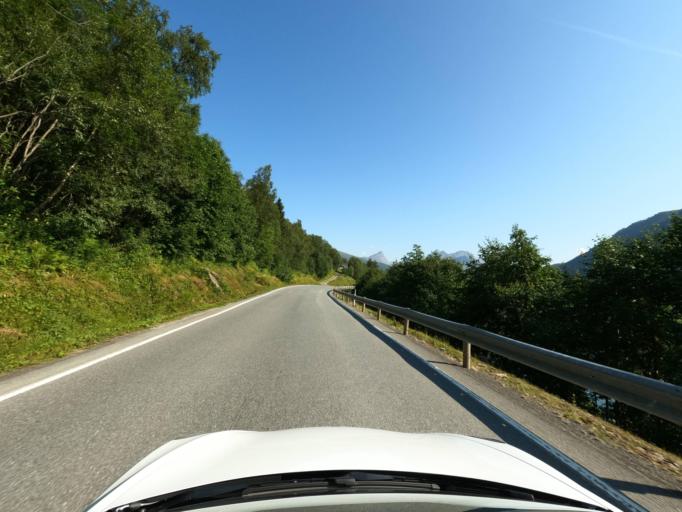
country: NO
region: Nordland
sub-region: Narvik
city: Narvik
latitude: 68.3921
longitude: 17.5369
